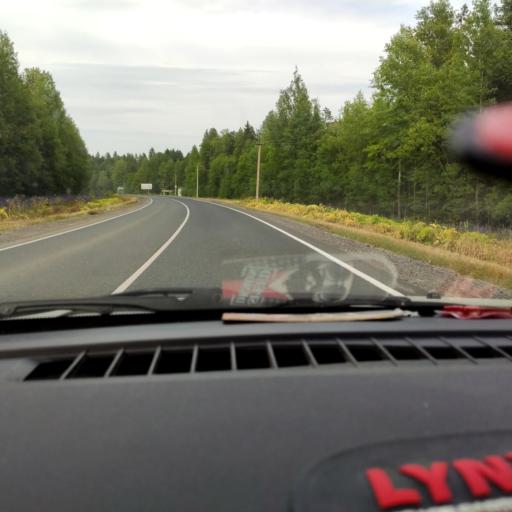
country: RU
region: Perm
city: Polazna
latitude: 58.1961
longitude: 56.2775
